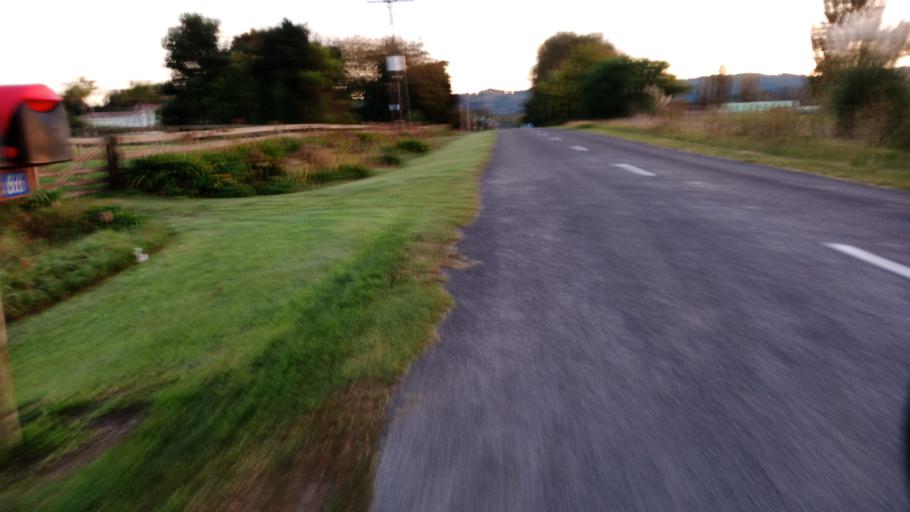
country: NZ
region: Gisborne
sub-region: Gisborne District
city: Gisborne
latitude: -38.6392
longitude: 177.9839
